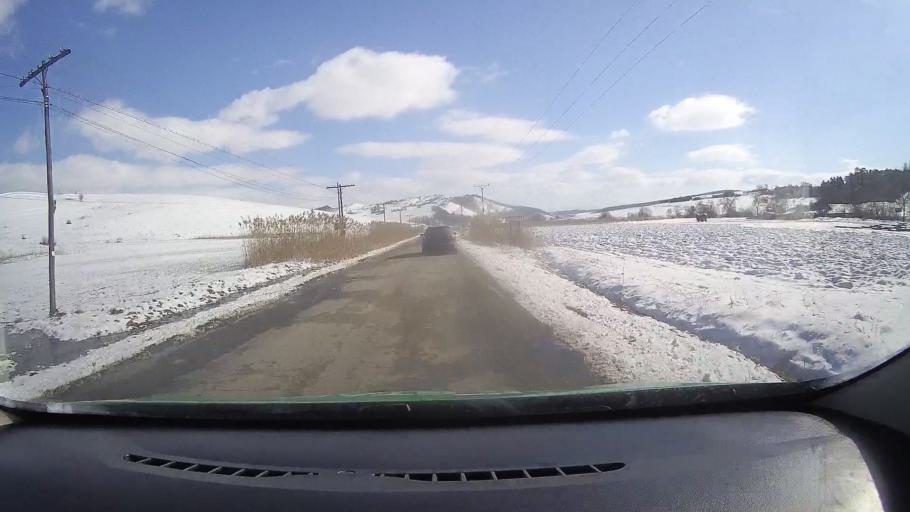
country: RO
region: Sibiu
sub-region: Comuna Altina
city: Altina
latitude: 45.9812
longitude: 24.4590
